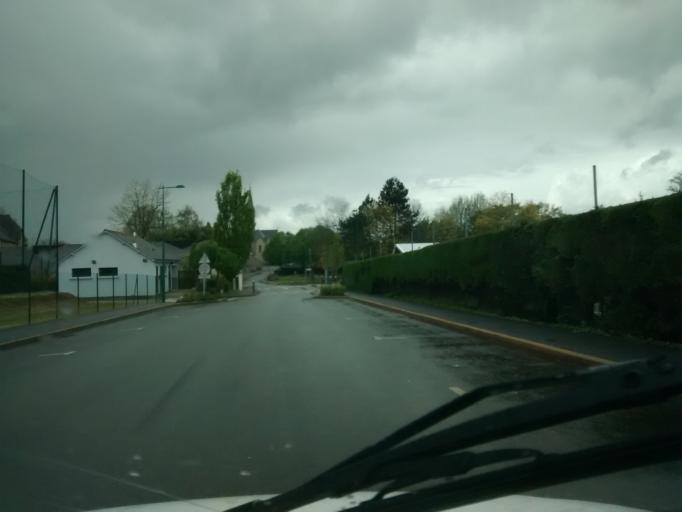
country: FR
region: Brittany
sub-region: Departement du Morbihan
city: Pleucadeuc
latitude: 47.7589
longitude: -2.3718
